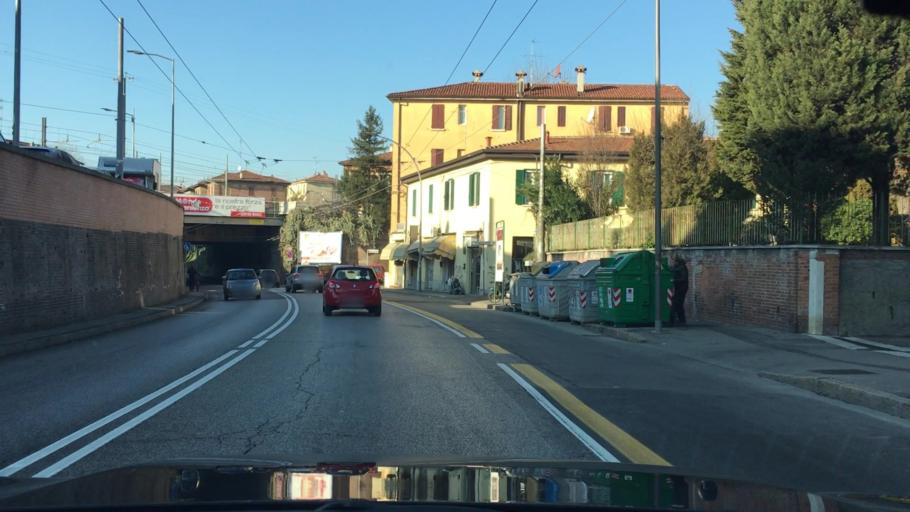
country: IT
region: Emilia-Romagna
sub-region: Provincia di Bologna
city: Ponticella
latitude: 44.4937
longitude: 11.3812
